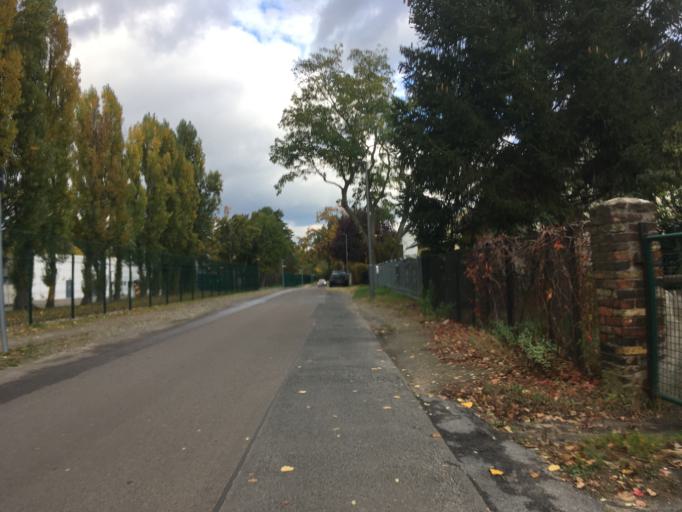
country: DE
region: Berlin
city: Adlershof
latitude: 52.4485
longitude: 13.5535
